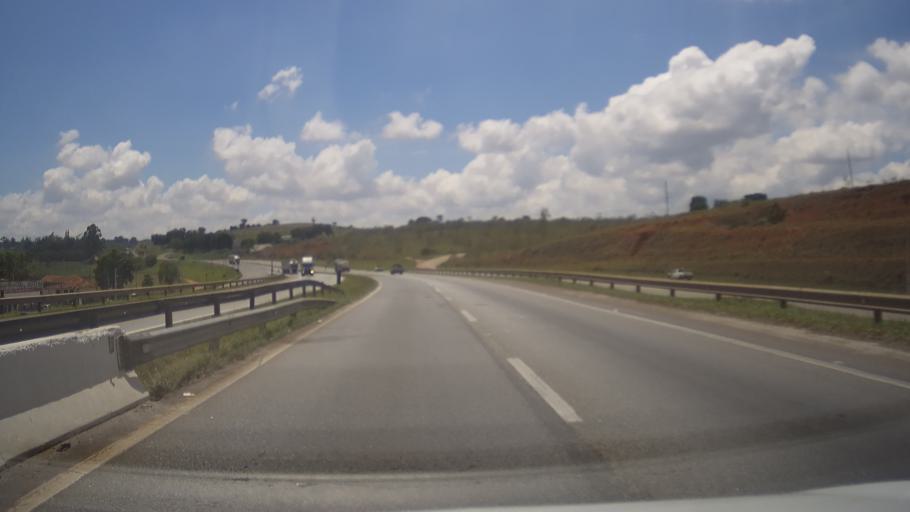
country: BR
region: Minas Gerais
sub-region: Sao Goncalo Do Sapucai
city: Sao Goncalo do Sapucai
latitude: -21.9142
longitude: -45.5785
